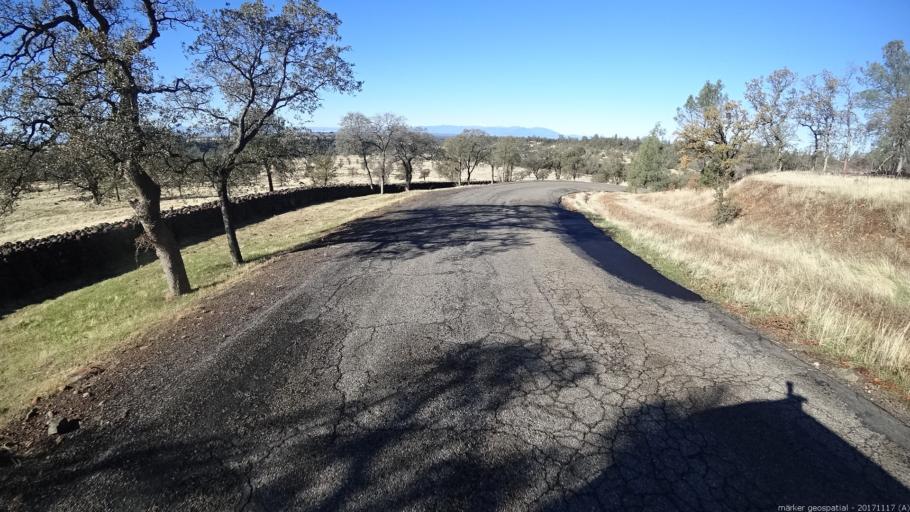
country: US
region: California
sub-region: Shasta County
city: Cottonwood
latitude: 40.4380
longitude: -122.1223
